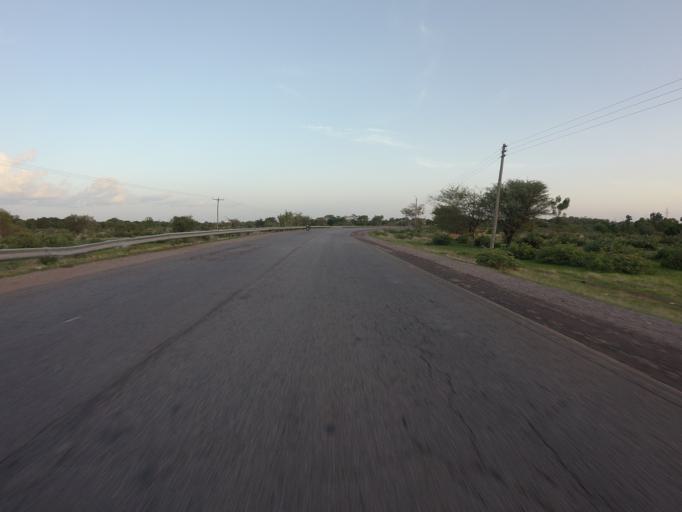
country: GH
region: Upper East
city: Navrongo
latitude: 10.9329
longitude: -1.0890
